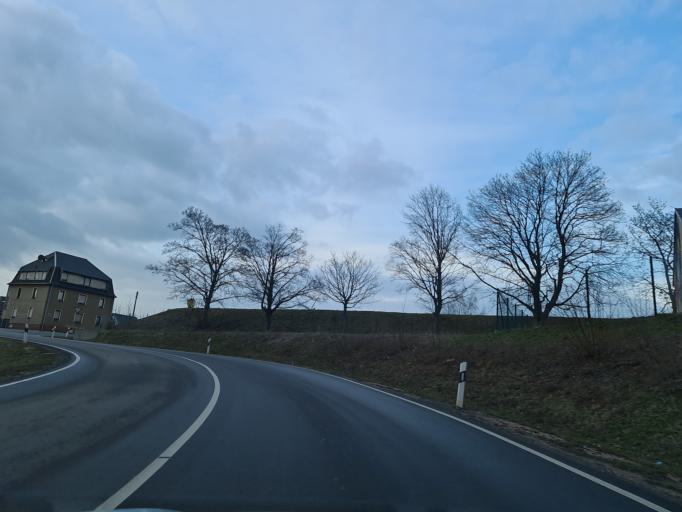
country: DE
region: Saxony
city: Mulsen
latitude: 50.7277
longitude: 12.5566
